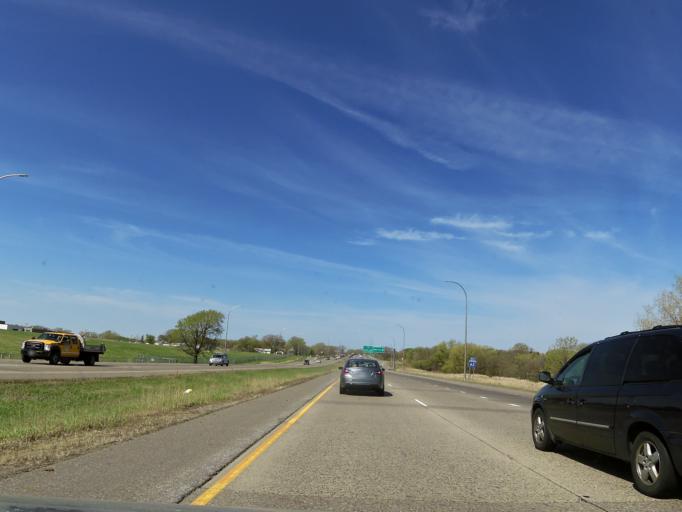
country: US
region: Minnesota
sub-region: Hennepin County
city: Richfield
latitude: 44.8974
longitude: -93.2256
